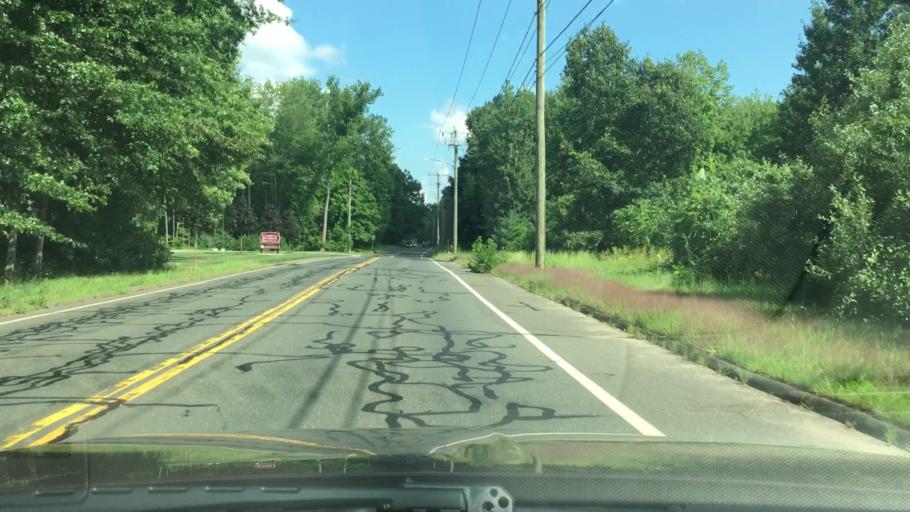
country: US
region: Connecticut
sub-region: Hartford County
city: South Windsor
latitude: 41.8298
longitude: -72.5954
